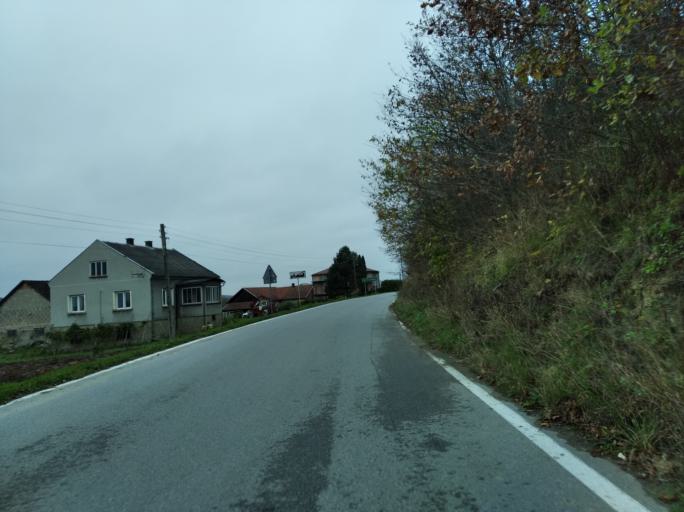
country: PL
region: Subcarpathian Voivodeship
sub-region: Powiat krosnienski
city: Leki
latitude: 49.8268
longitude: 21.6388
